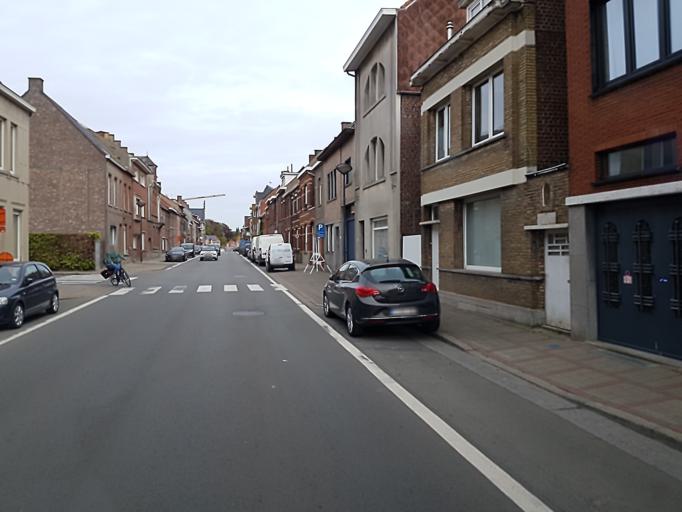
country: BE
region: Flanders
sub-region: Provincie West-Vlaanderen
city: Tielt
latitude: 50.9970
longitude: 3.3275
